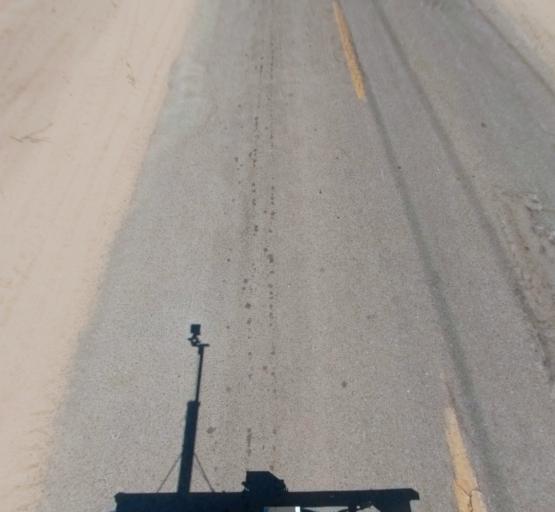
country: US
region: California
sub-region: Madera County
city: Fairmead
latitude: 37.1348
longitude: -120.2021
